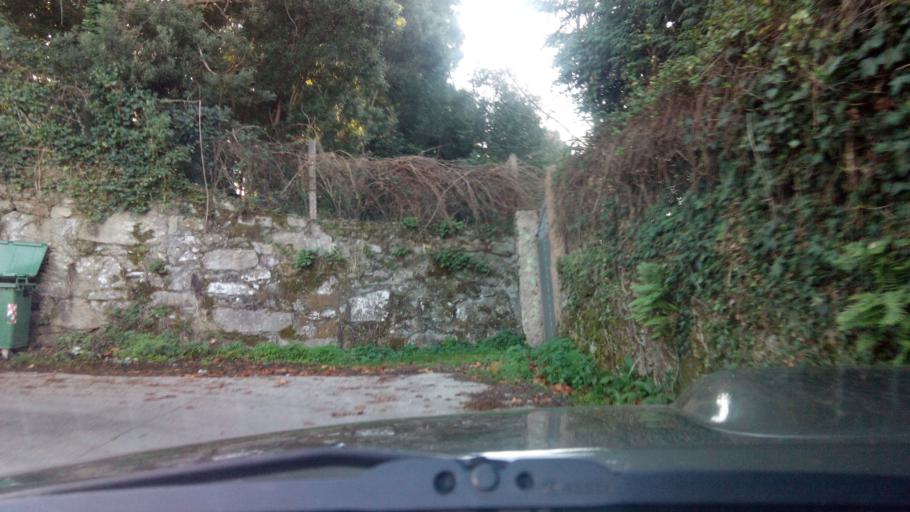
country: ES
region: Galicia
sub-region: Provincia de Pontevedra
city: Marin
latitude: 42.3613
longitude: -8.7001
